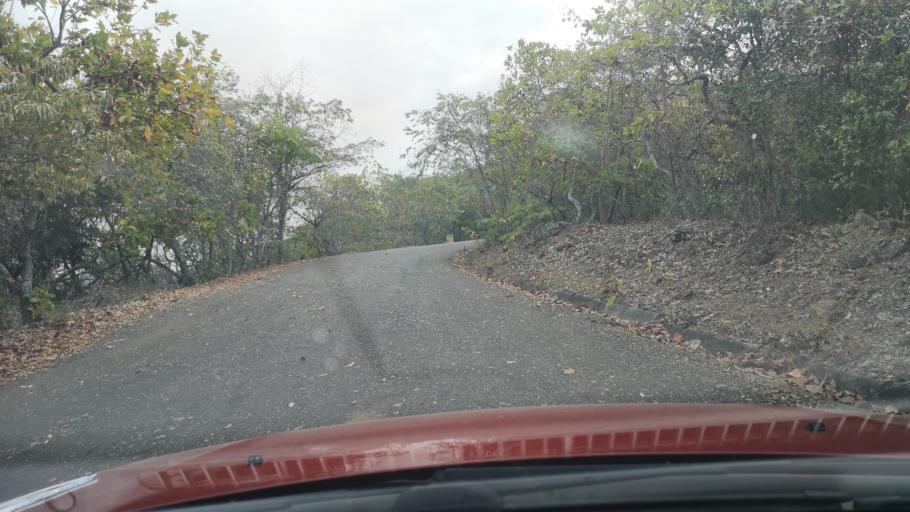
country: CO
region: Huila
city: Neiva
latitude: 2.9577
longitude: -75.3469
